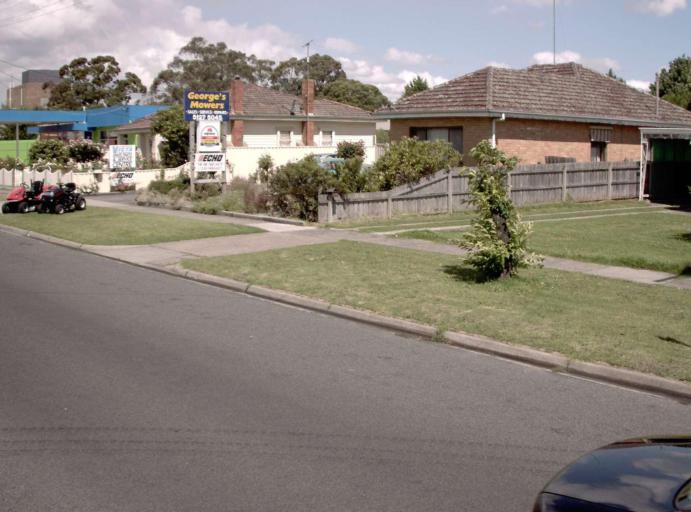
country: AU
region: Victoria
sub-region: Latrobe
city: Moe
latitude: -38.1776
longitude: 146.2583
